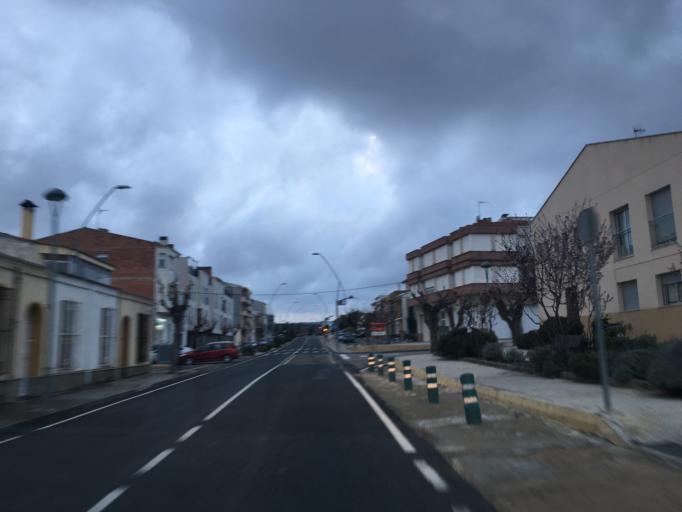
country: ES
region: Catalonia
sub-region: Provincia de Tarragona
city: la Bisbal del Penedes
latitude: 41.2778
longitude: 1.4922
